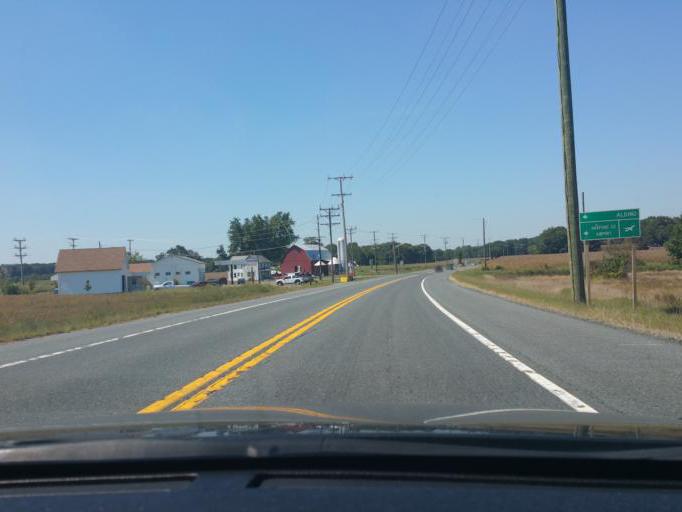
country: US
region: Maryland
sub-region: Harford County
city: Aberdeen
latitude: 39.5722
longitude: -76.1734
